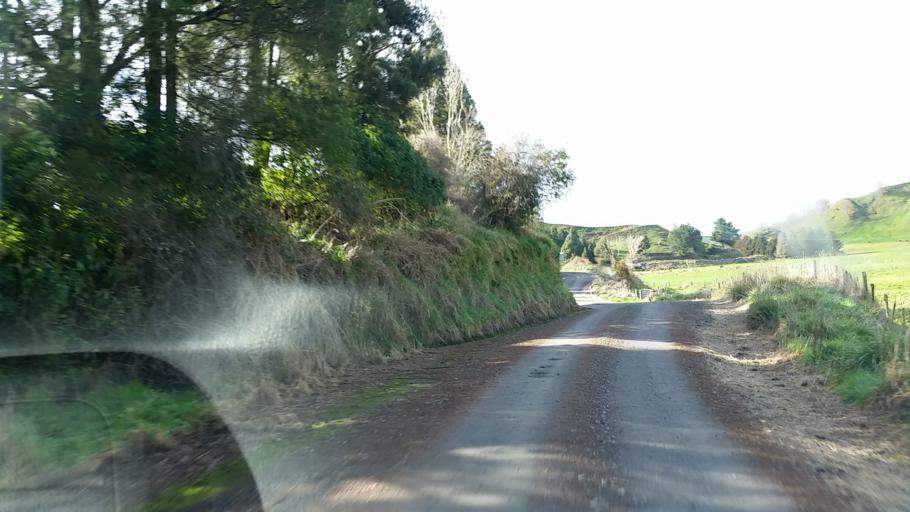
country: NZ
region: Taranaki
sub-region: South Taranaki District
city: Eltham
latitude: -39.2550
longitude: 174.5195
